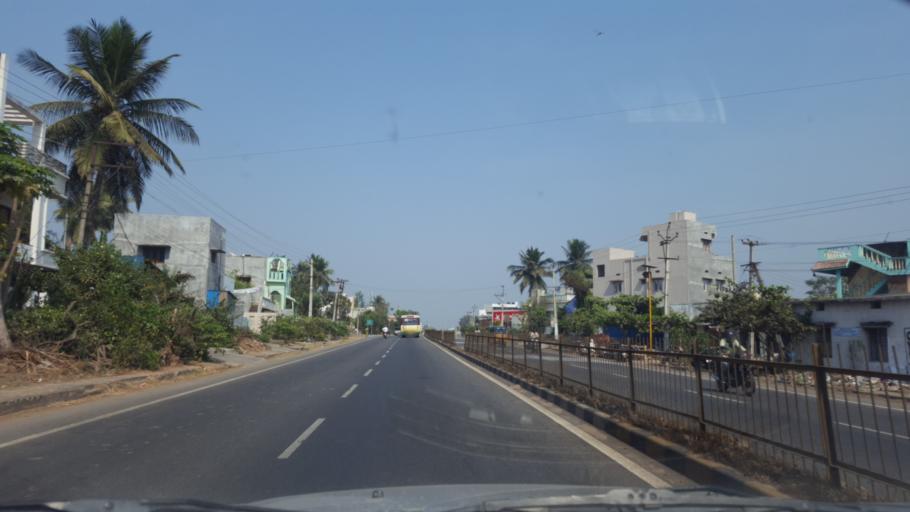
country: IN
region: Andhra Pradesh
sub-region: Vishakhapatnam
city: Anakapalle
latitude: 17.6785
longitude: 82.9780
